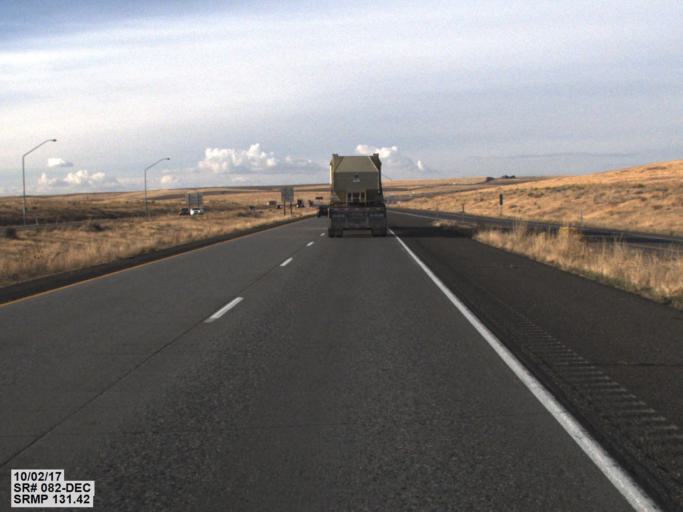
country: US
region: Oregon
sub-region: Umatilla County
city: Umatilla
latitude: 45.9478
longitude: -119.3361
